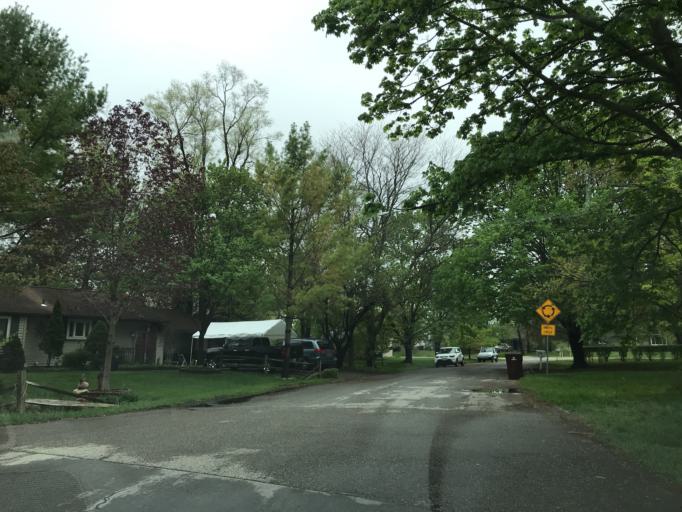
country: US
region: Michigan
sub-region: Washtenaw County
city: Ann Arbor
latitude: 42.2479
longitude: -83.7072
